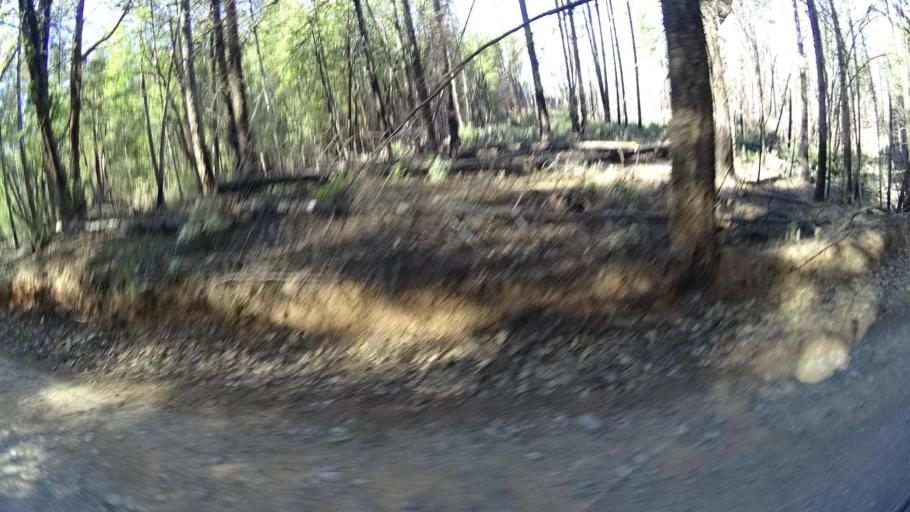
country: US
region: California
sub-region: Lake County
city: Upper Lake
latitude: 39.3543
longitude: -122.9788
